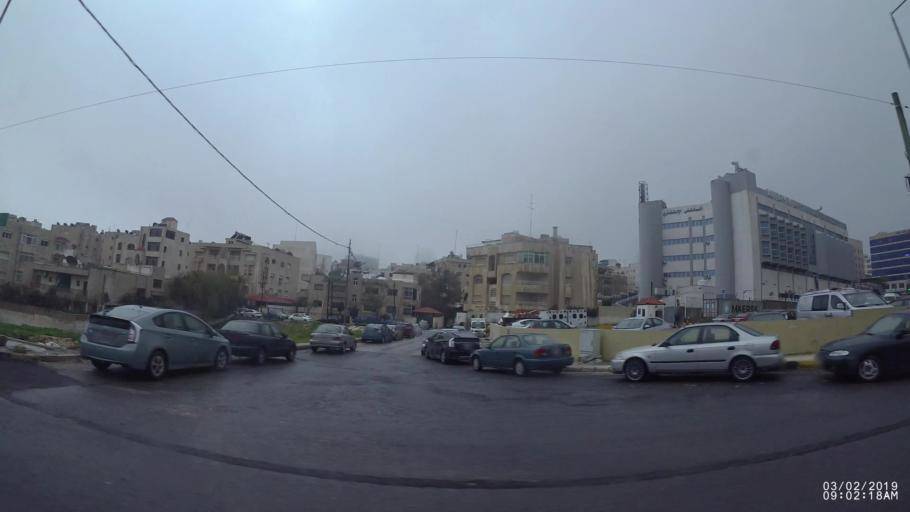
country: JO
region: Amman
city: Amman
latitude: 31.9653
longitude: 35.8876
